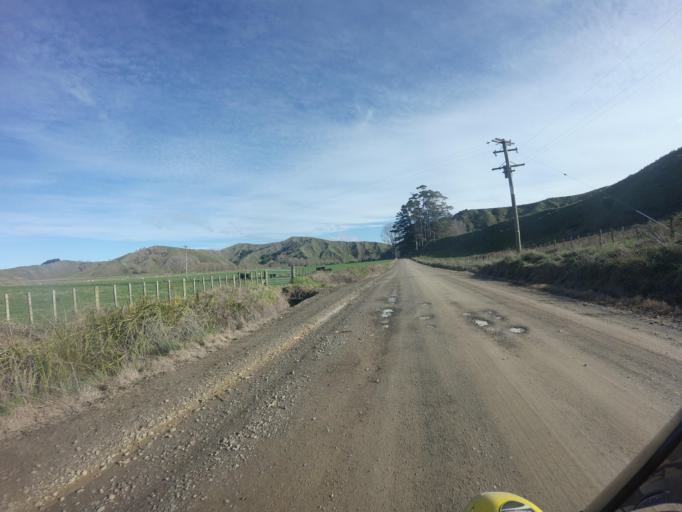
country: NZ
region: Hawke's Bay
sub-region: Wairoa District
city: Wairoa
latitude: -39.0261
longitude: 177.5786
